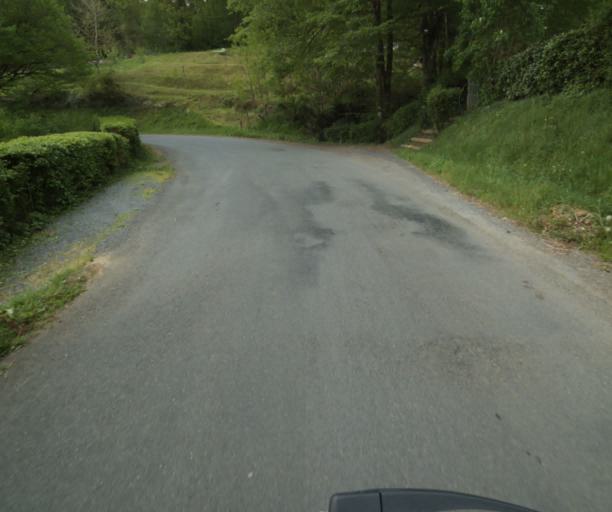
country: FR
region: Limousin
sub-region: Departement de la Correze
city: Tulle
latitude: 45.2809
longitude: 1.7648
